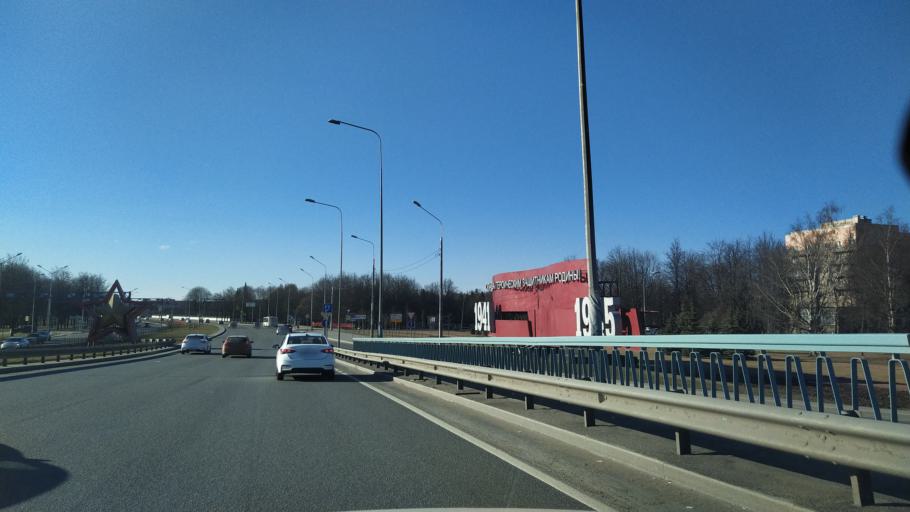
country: RU
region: Leningrad
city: Kalininskiy
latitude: 59.9926
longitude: 30.4298
